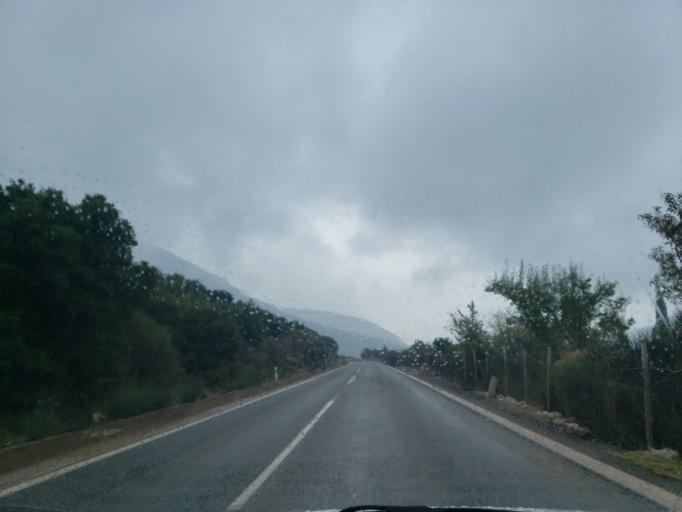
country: GR
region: Central Greece
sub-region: Nomos Fokidos
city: Amfissa
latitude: 38.5910
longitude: 22.3846
